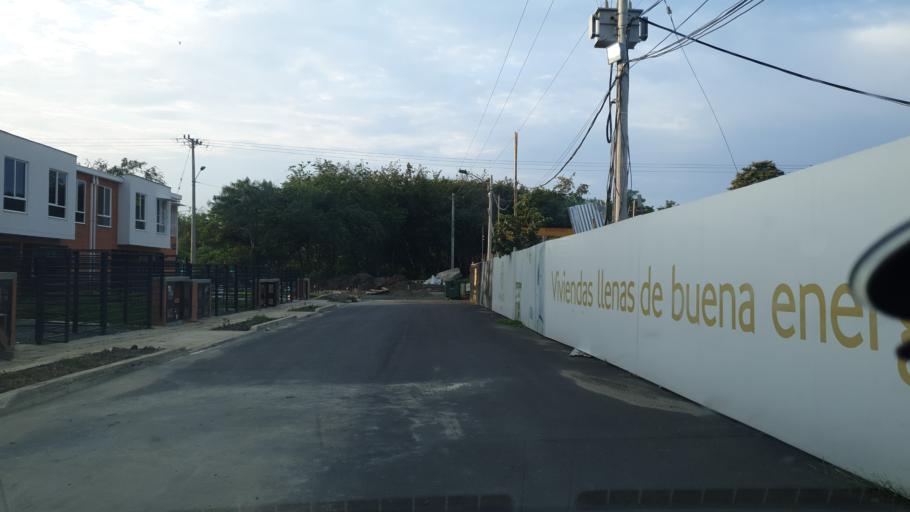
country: CO
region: Valle del Cauca
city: Jamundi
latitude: 3.3465
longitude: -76.5183
